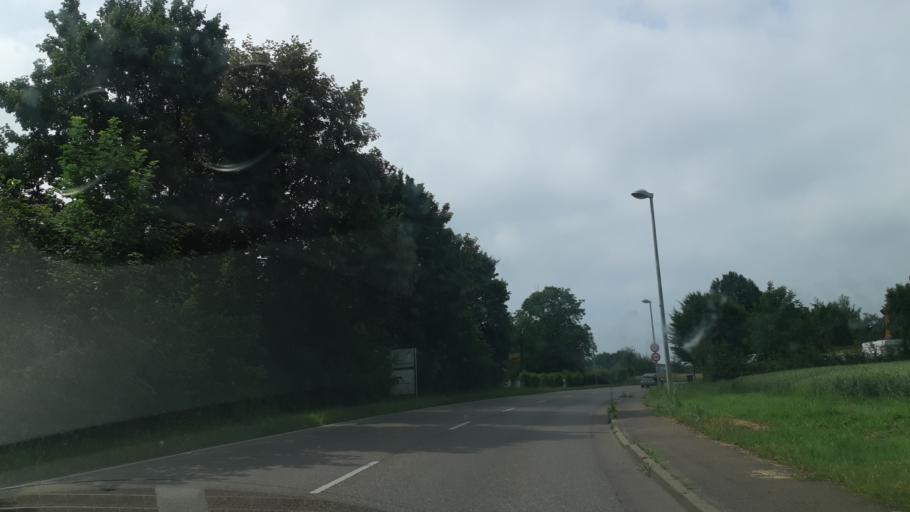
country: DE
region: Baden-Wuerttemberg
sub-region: Regierungsbezirk Stuttgart
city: Heiningen
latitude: 48.6817
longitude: 9.6260
